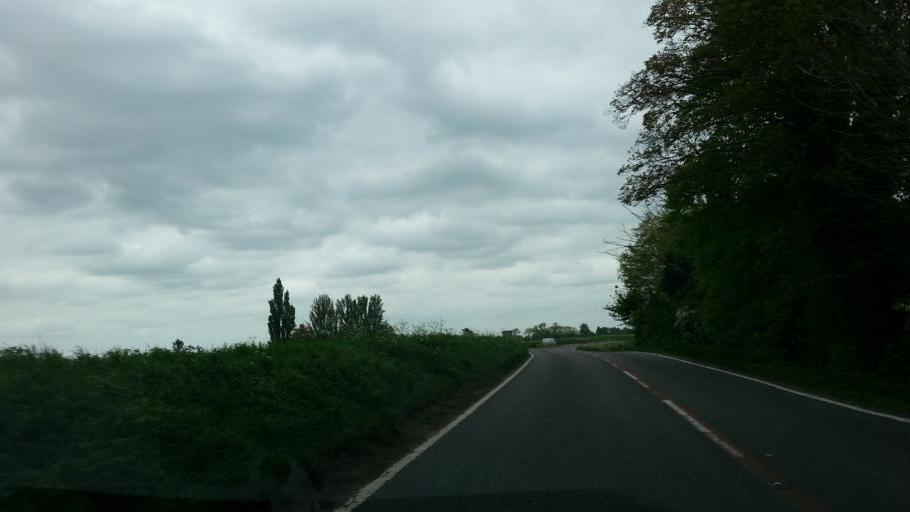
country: GB
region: England
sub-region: Cambridgeshire
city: Littleport
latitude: 52.4846
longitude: 0.3458
